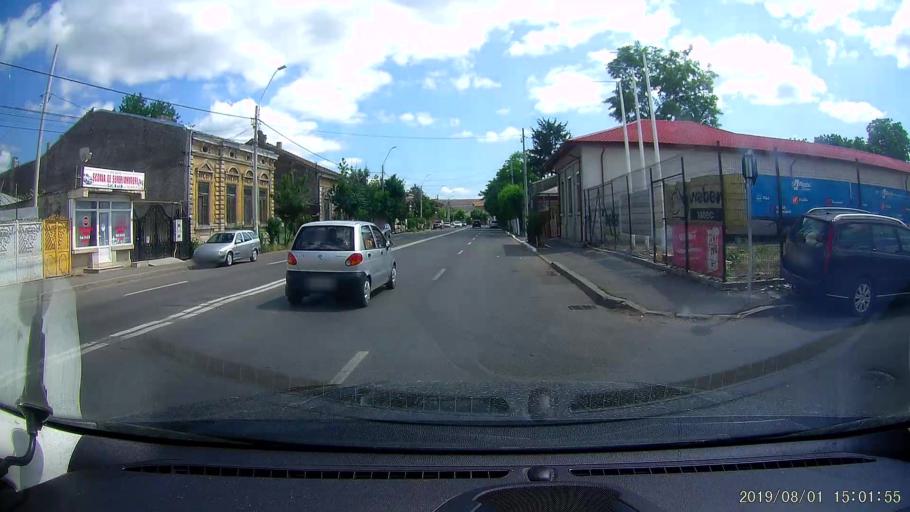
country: RO
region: Braila
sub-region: Municipiul Braila
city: Braila
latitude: 45.2703
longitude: 27.9603
